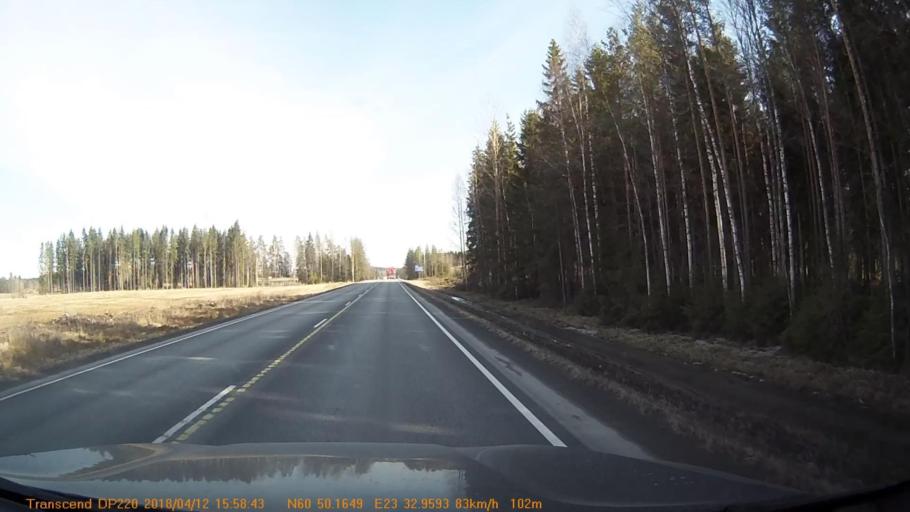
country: FI
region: Haeme
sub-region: Forssa
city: Forssa
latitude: 60.8355
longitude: 23.5507
